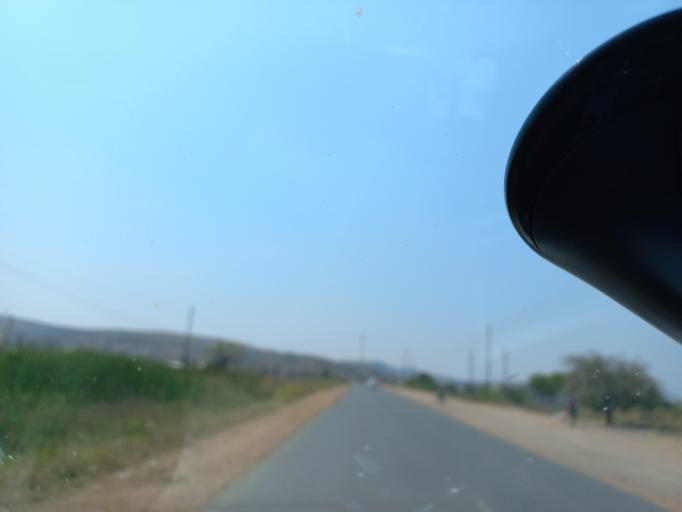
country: ZM
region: Lusaka
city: Kafue
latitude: -15.7573
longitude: 28.1723
